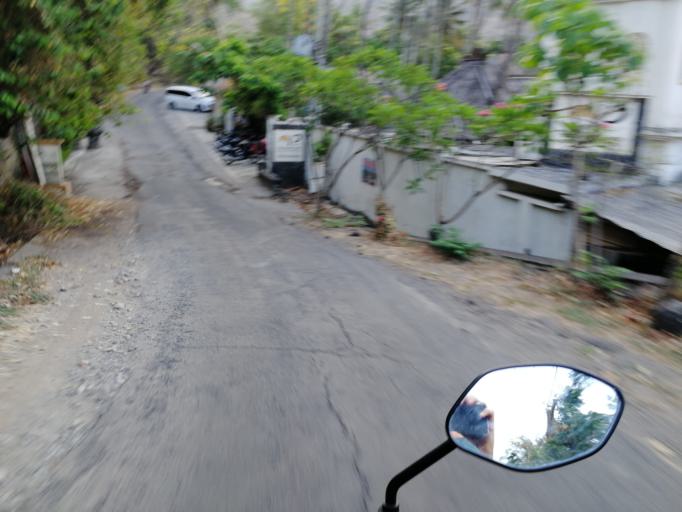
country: ID
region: Bali
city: Biaslantang Kaler
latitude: -8.3562
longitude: 115.6911
